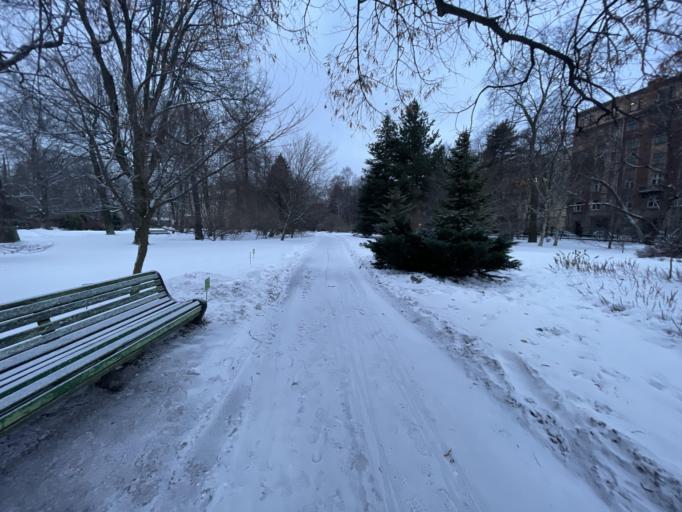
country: RU
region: St.-Petersburg
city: Petrogradka
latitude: 59.9702
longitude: 30.3199
